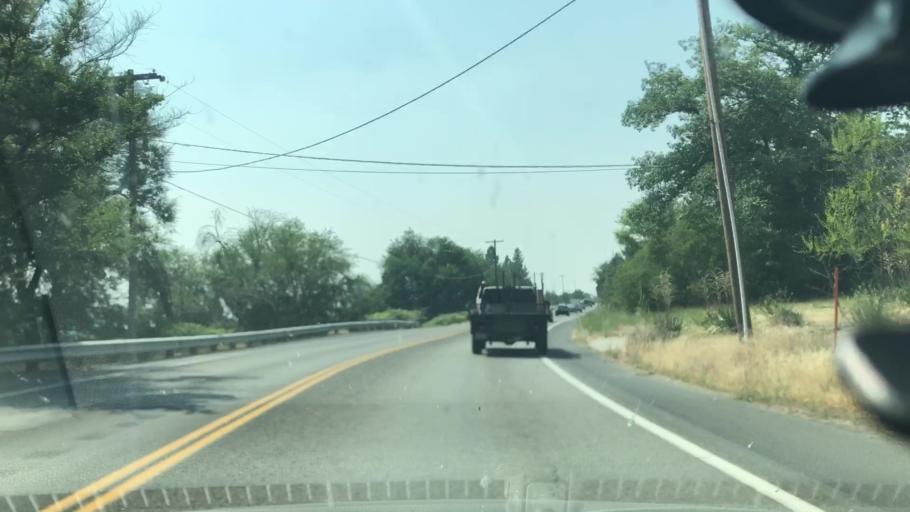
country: US
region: Washington
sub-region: Spokane County
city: Millwood
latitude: 47.6875
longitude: -117.3235
